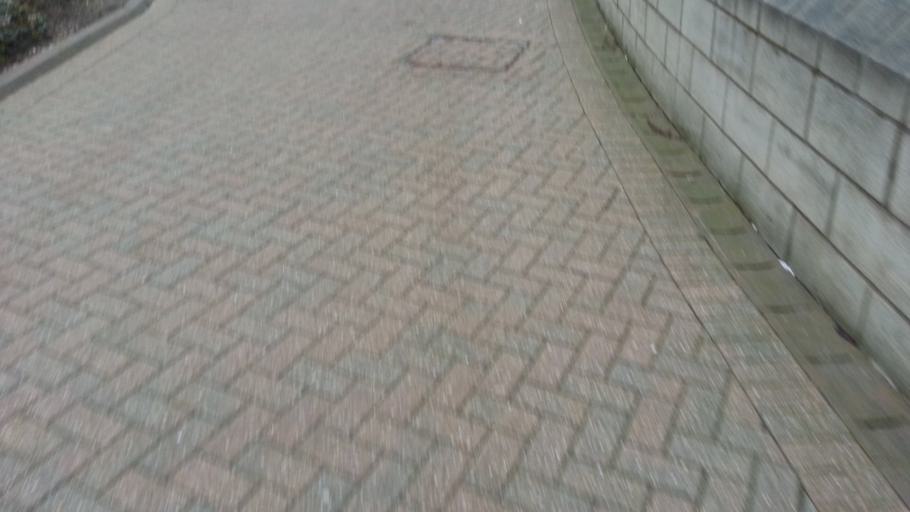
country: GB
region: England
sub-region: Reading
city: Reading
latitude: 51.4604
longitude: -0.9684
